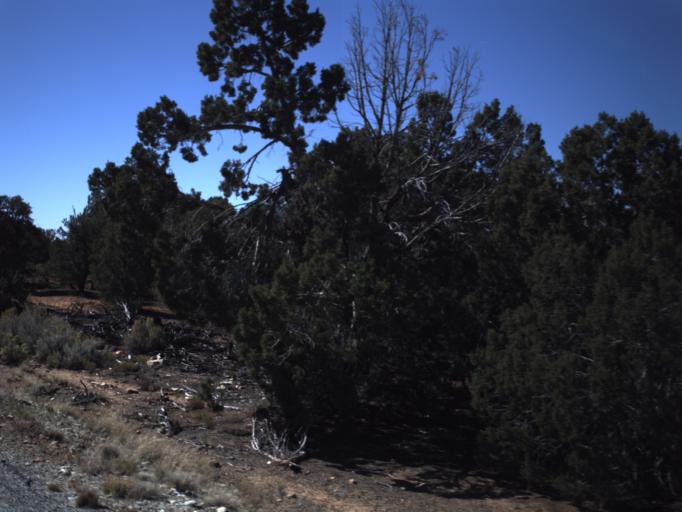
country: US
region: Utah
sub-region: San Juan County
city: Blanding
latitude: 37.4210
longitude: -109.9428
